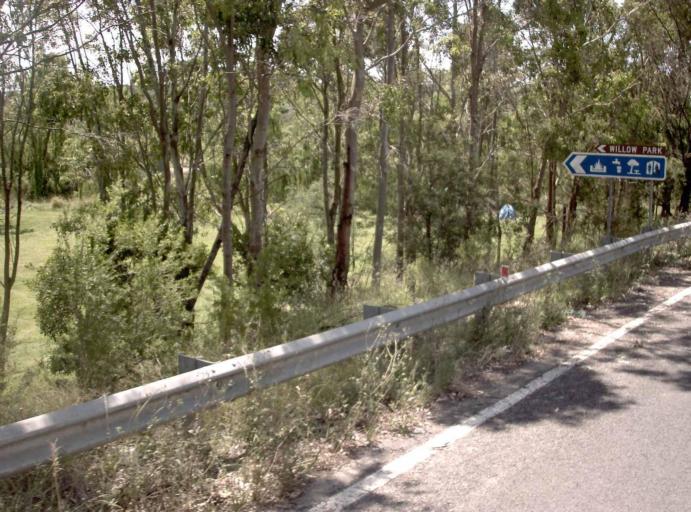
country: AU
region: Victoria
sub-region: Wellington
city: Heyfield
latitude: -38.1418
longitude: 146.7927
